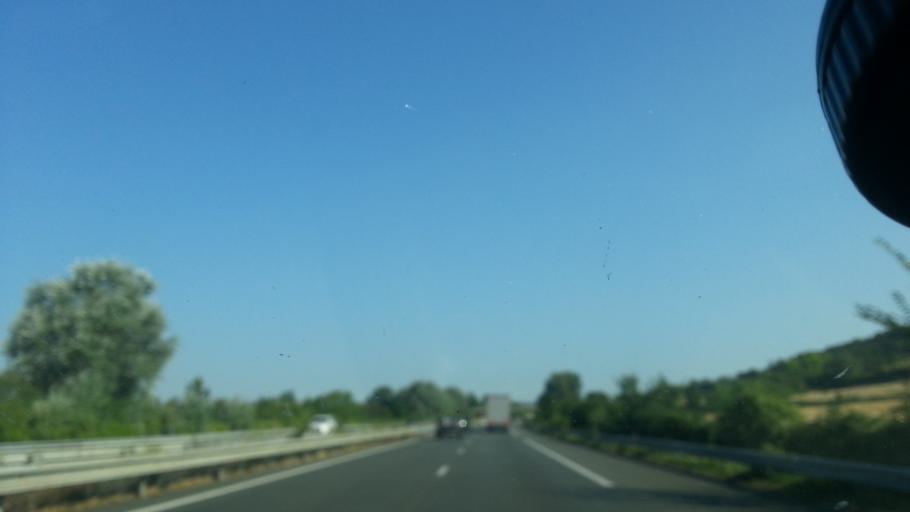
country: FR
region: Poitou-Charentes
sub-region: Departement de la Vienne
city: Antran
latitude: 46.8740
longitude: 0.5202
